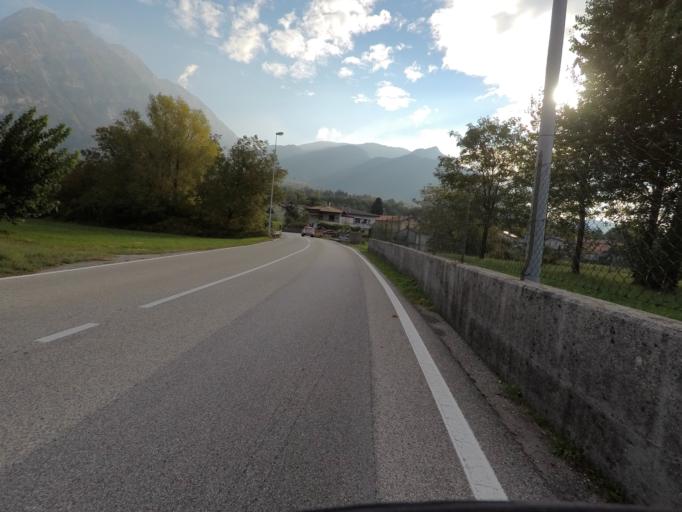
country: IT
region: Friuli Venezia Giulia
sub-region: Provincia di Udine
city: Gemona
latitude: 46.2857
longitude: 13.1265
